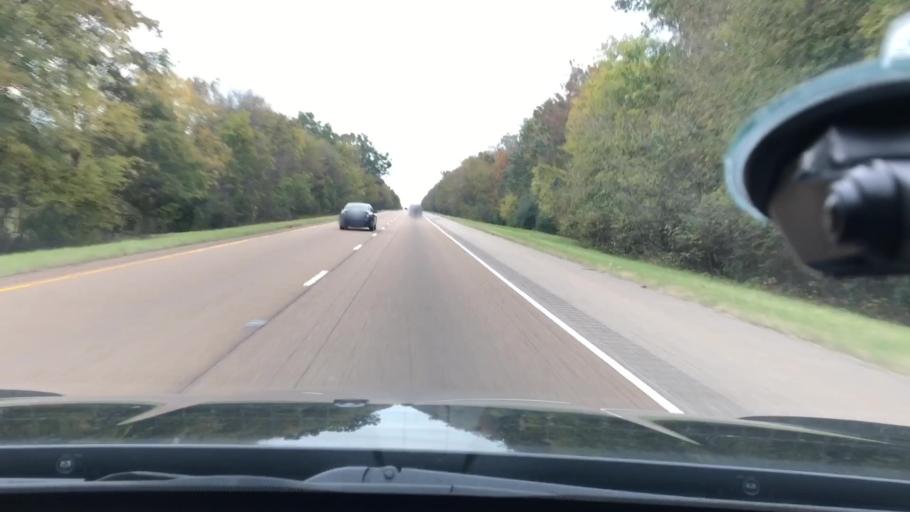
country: US
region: Arkansas
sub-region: Nevada County
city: Prescott
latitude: 33.8015
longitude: -93.4354
